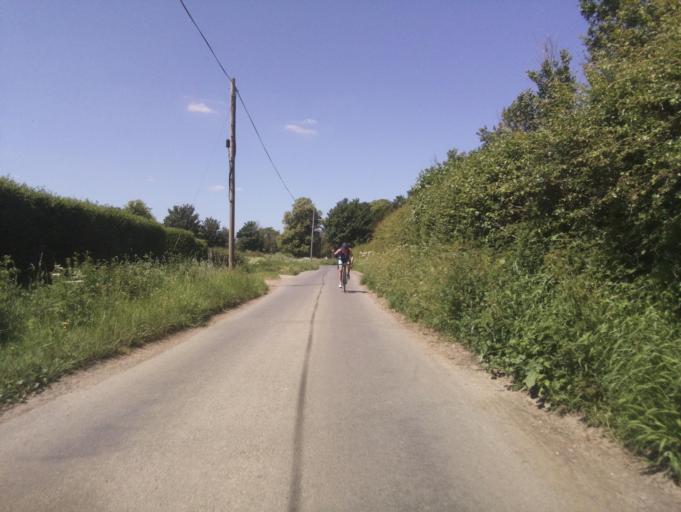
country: GB
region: England
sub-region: Wiltshire
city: Bremhill
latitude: 51.4666
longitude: -2.0754
